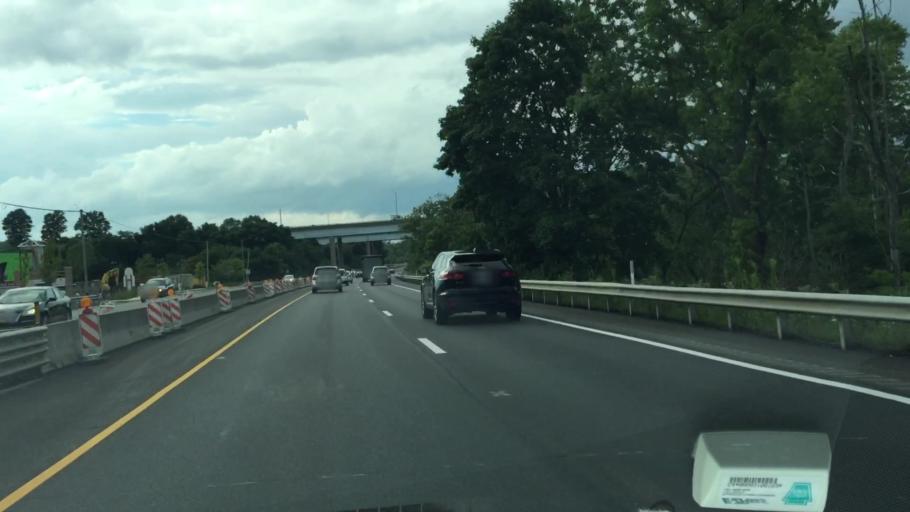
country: US
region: Pennsylvania
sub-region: Allegheny County
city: Bradford Woods
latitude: 40.6564
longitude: -80.0886
